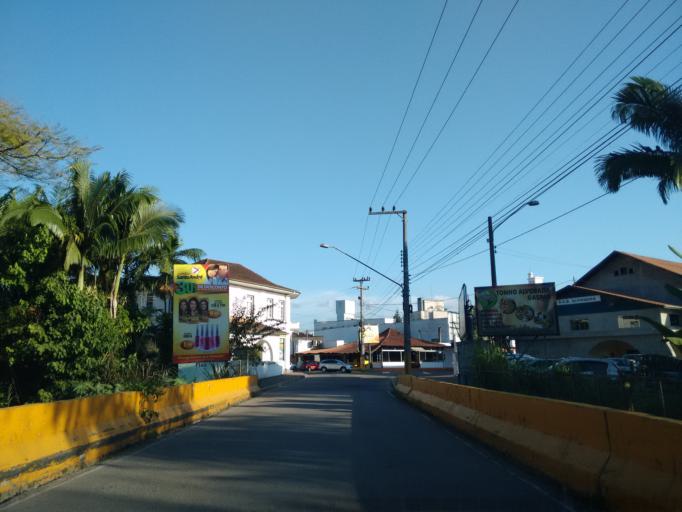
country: BR
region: Santa Catarina
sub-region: Gaspar
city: Gaspar
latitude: -26.9269
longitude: -48.9524
